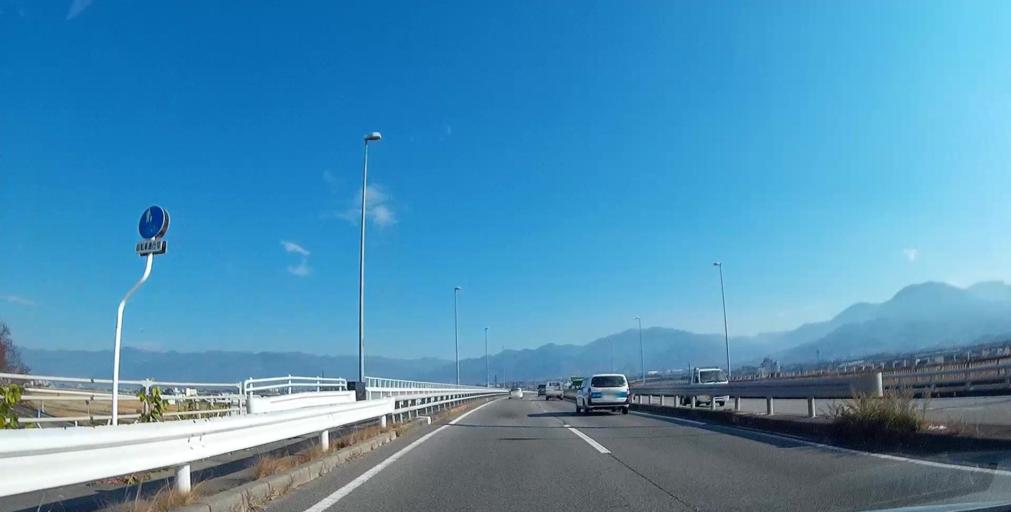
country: JP
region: Yamanashi
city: Isawa
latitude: 35.6439
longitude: 138.6369
